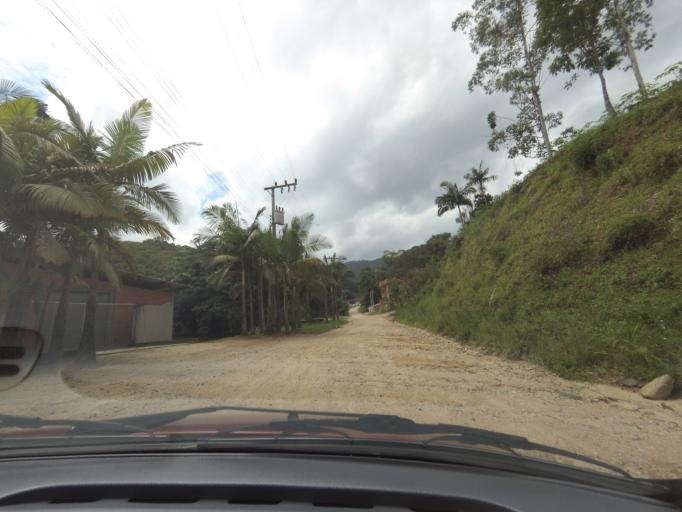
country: BR
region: Santa Catarina
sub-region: Brusque
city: Brusque
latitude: -27.0578
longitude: -48.9950
